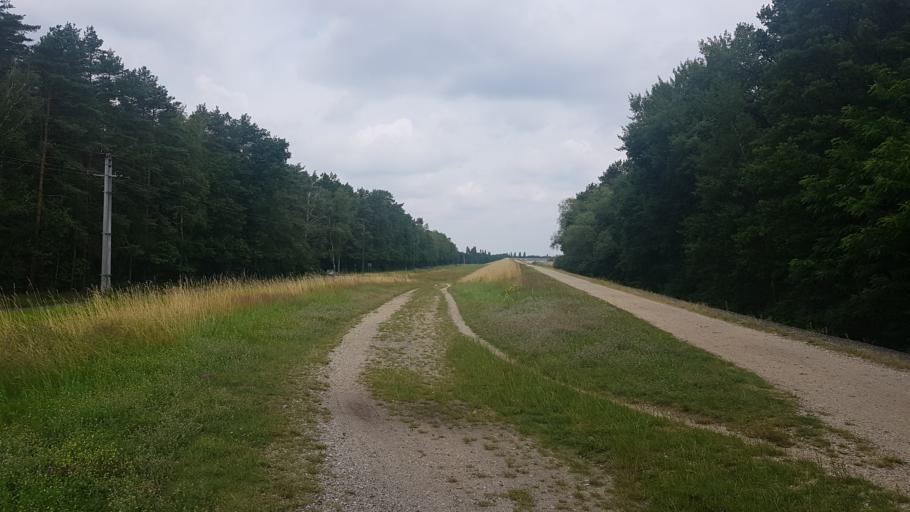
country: PL
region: Opole Voivodeship
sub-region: Powiat opolski
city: Chrzastowice
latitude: 50.7107
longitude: 18.0927
